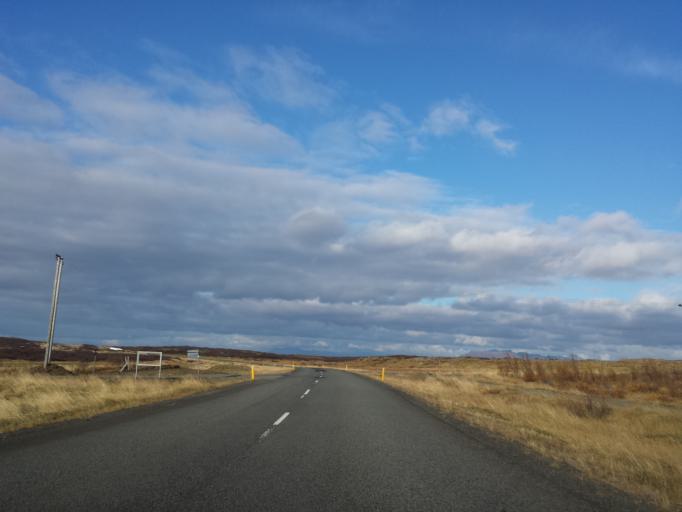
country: IS
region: West
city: Borgarnes
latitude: 64.5802
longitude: -21.9650
